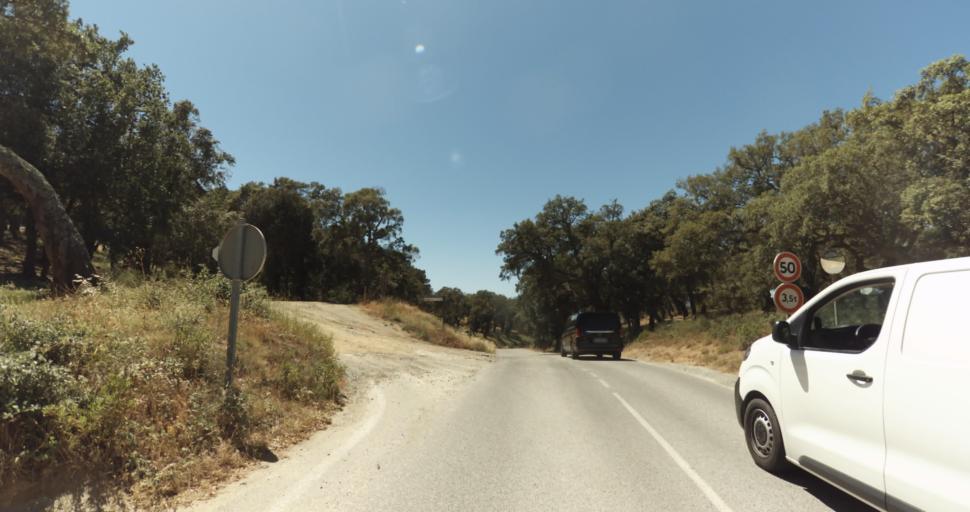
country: FR
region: Provence-Alpes-Cote d'Azur
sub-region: Departement du Var
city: Gassin
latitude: 43.2423
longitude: 6.5607
